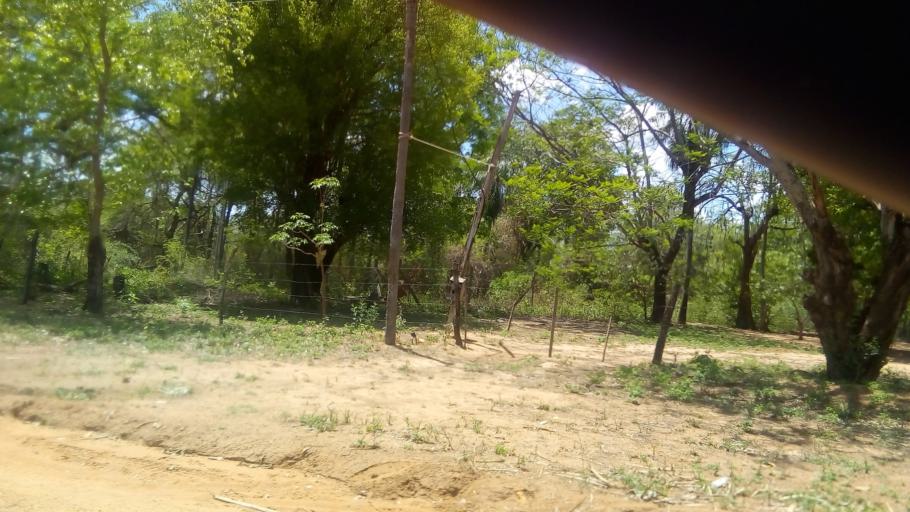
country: PY
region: Cordillera
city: Arroyos y Esteros
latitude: -24.9912
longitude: -57.2123
